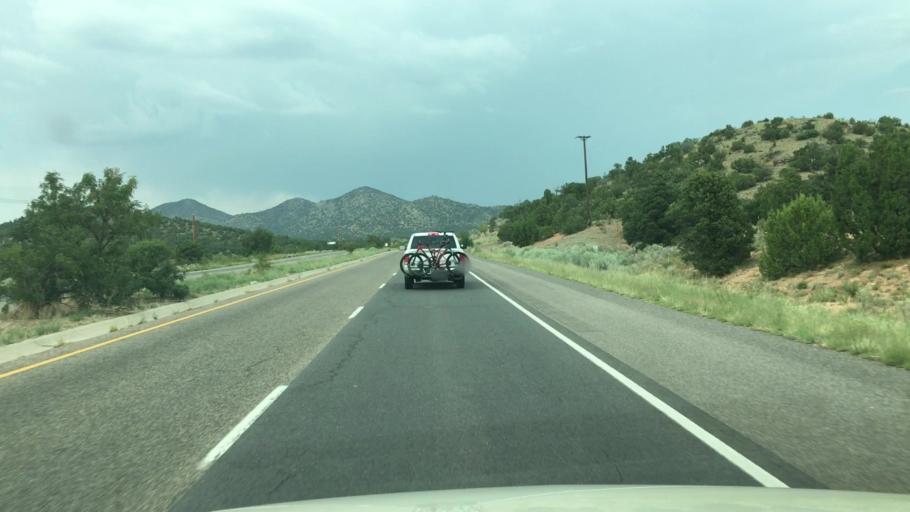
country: US
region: New Mexico
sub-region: Santa Fe County
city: Eldorado at Santa Fe
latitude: 35.5441
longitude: -105.8840
